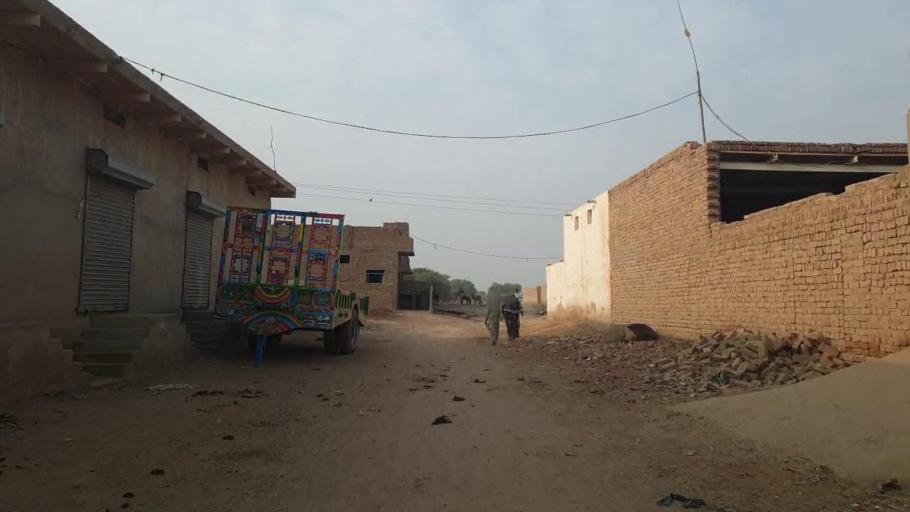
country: PK
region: Sindh
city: Sann
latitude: 26.1383
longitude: 68.0511
